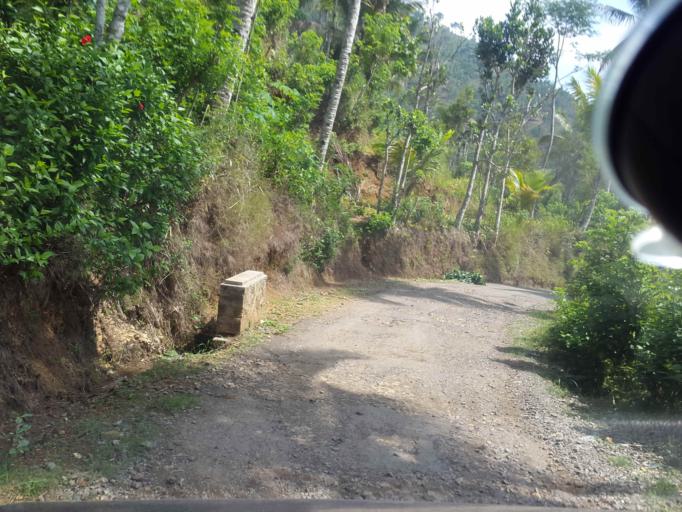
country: ID
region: East Java
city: Sidem
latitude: -8.1048
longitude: 111.5881
